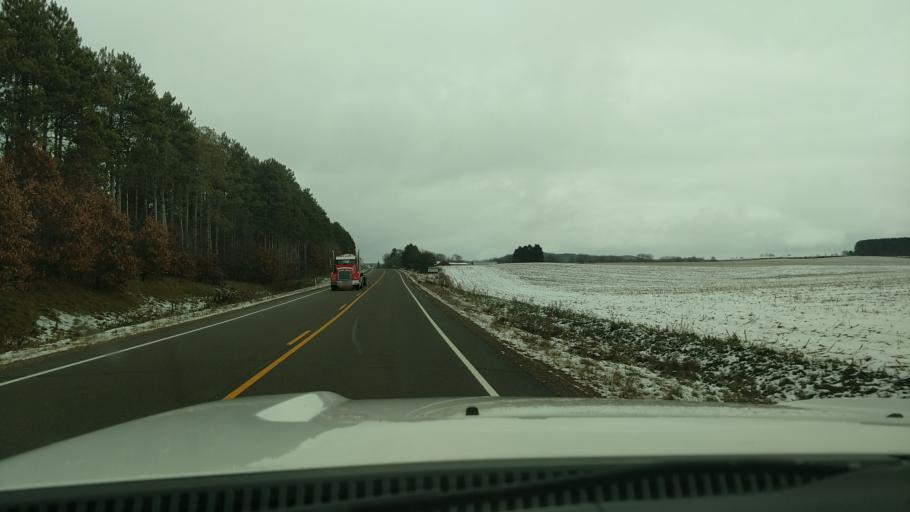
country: US
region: Wisconsin
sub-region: Dunn County
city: Colfax
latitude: 45.1426
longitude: -91.6713
